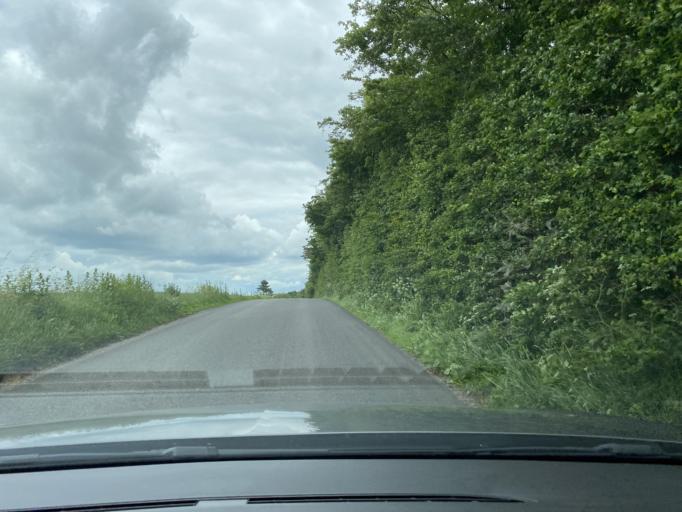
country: DK
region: South Denmark
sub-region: Vejle Kommune
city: Vejle
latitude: 55.6634
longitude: 9.4845
